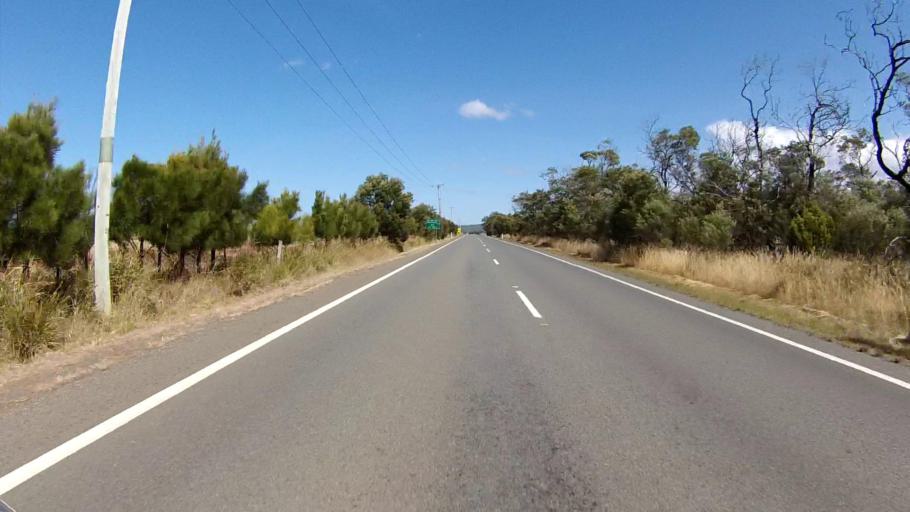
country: AU
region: Tasmania
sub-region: Break O'Day
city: St Helens
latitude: -42.0948
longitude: 148.0645
